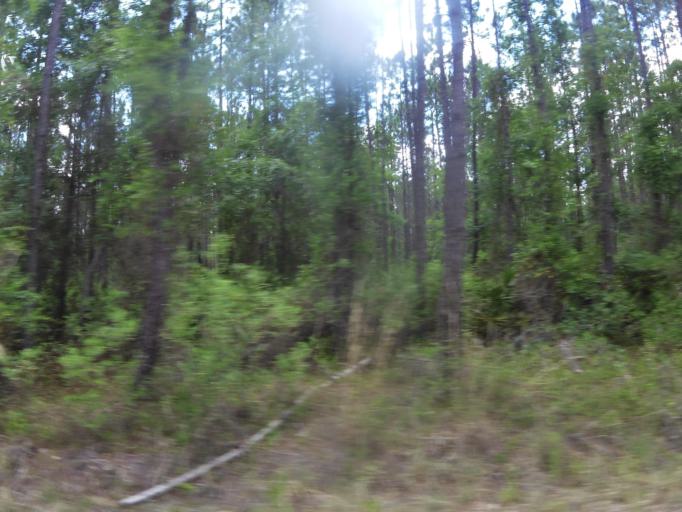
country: US
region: Florida
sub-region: Clay County
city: Asbury Lake
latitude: 29.8862
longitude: -81.8526
